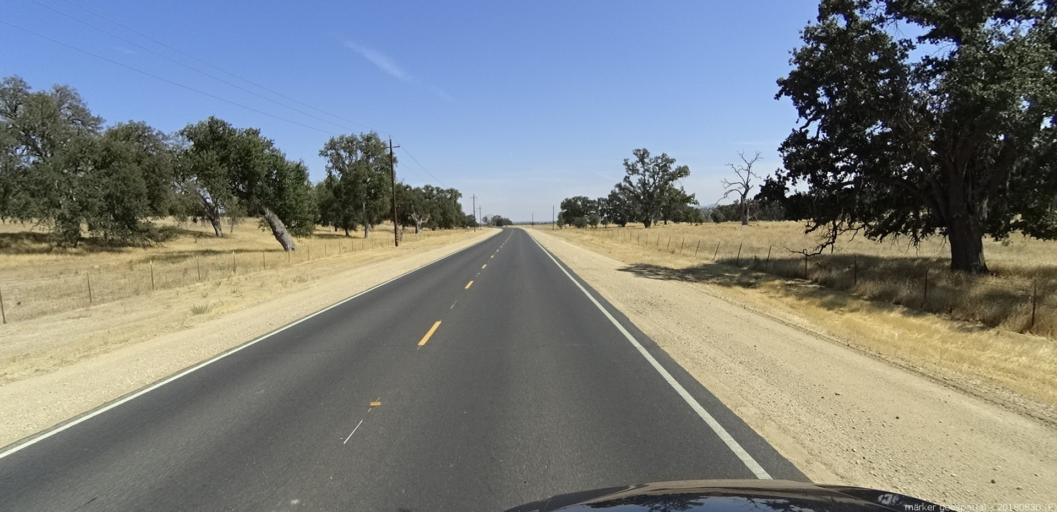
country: US
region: California
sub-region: Monterey County
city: King City
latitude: 35.9759
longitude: -121.2110
